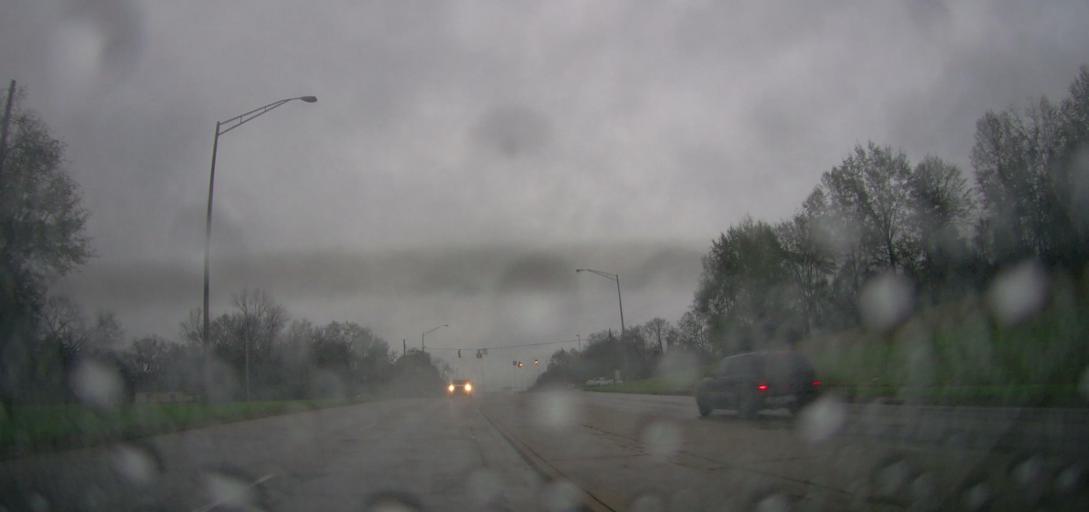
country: US
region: Alabama
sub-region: Montgomery County
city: Montgomery
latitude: 32.3695
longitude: -86.3309
